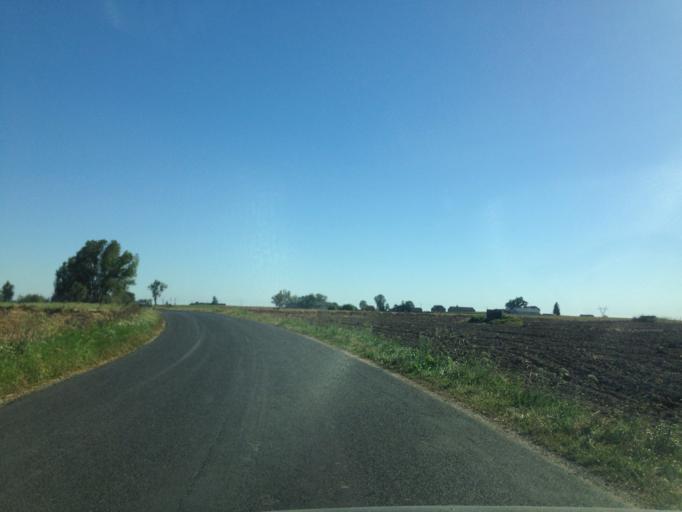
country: PL
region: Kujawsko-Pomorskie
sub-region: Powiat brodnicki
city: Swiedziebnia
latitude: 53.1907
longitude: 19.5622
